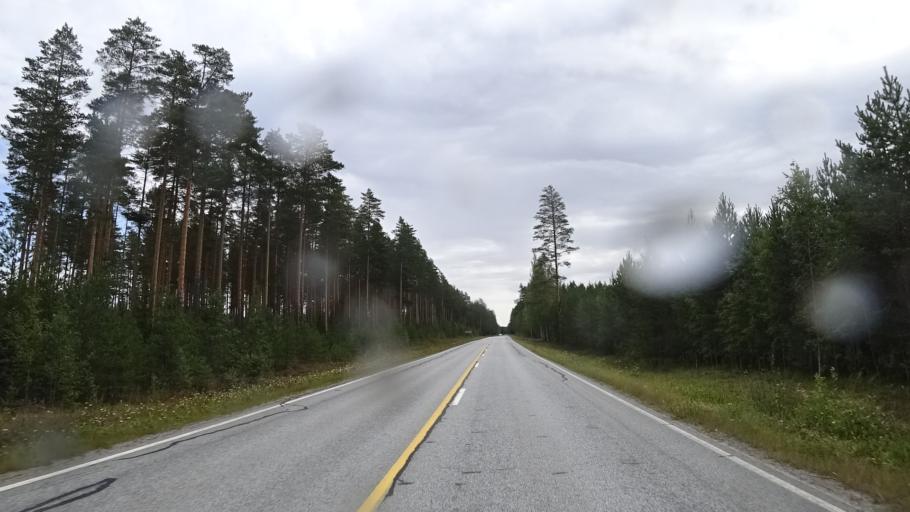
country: FI
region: North Karelia
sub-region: Keski-Karjala
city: Raeaekkylae
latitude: 62.1106
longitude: 29.7265
